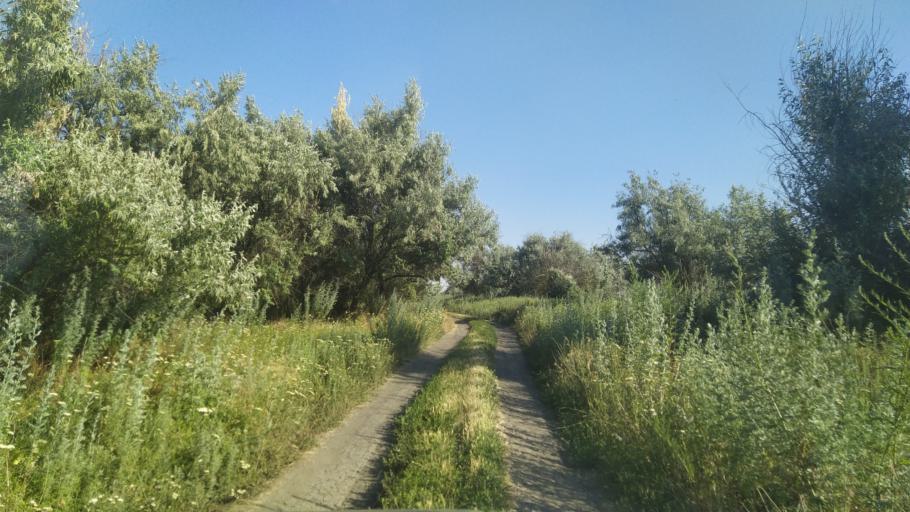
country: RU
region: Rostov
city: Kuleshovka
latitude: 47.1341
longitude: 39.6418
